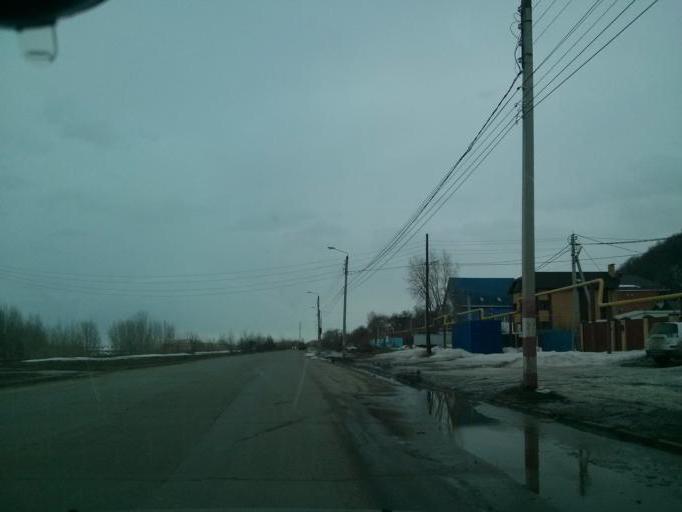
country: RU
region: Nizjnij Novgorod
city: Bor
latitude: 56.3111
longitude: 44.0900
